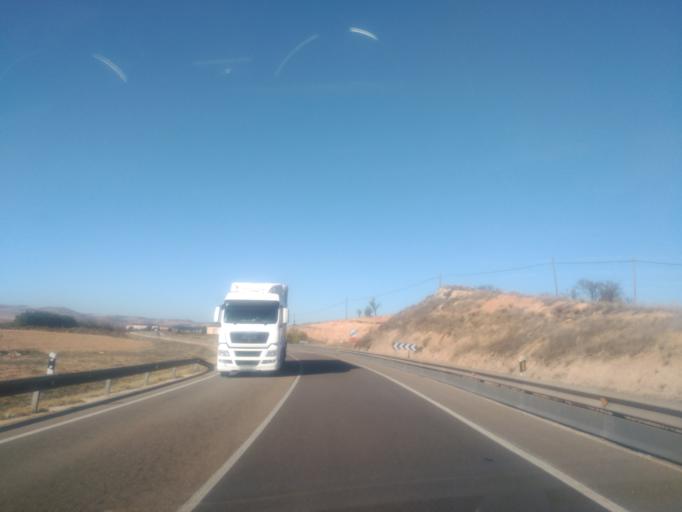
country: ES
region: Castille and Leon
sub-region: Provincia de Valladolid
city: Penafiel
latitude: 41.6079
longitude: -4.1435
